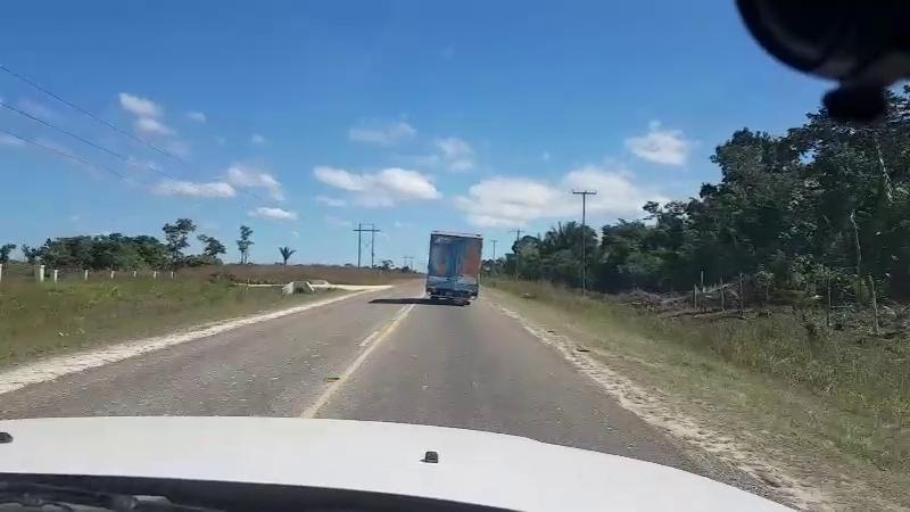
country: BZ
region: Cayo
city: Belmopan
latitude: 17.2767
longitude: -88.7387
